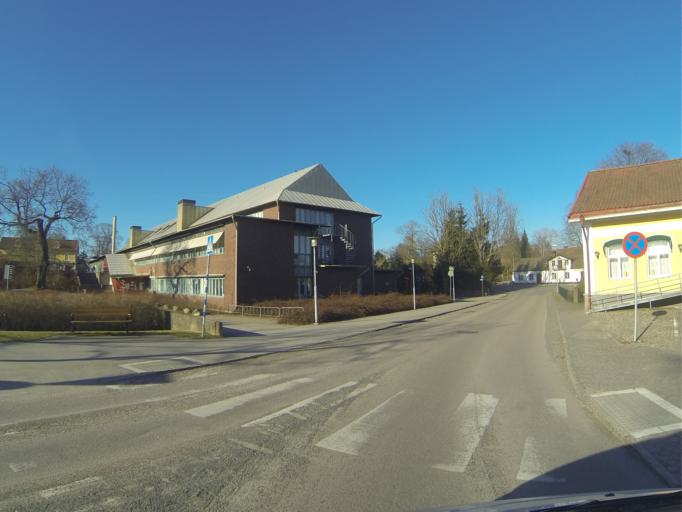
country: SE
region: Skane
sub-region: Hoors Kommun
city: Hoeoer
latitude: 55.9307
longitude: 13.5478
